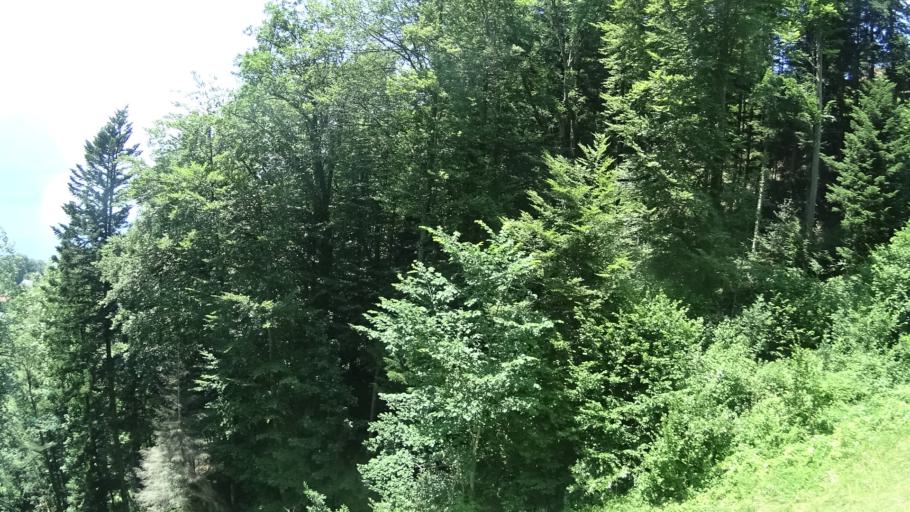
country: CH
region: Lucerne
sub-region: Lucerne-Land District
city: Vitznau
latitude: 47.0230
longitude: 8.4844
